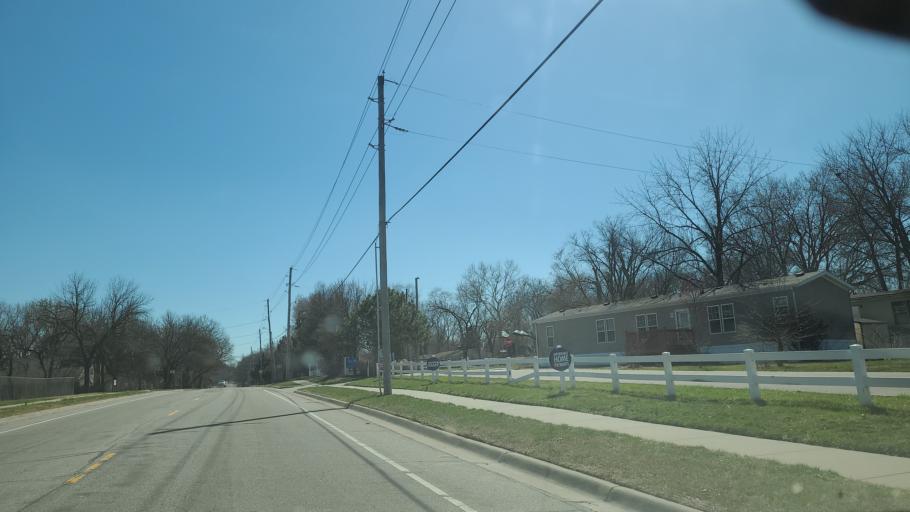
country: US
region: Kansas
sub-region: Douglas County
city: Lawrence
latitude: 38.9835
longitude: -95.2512
